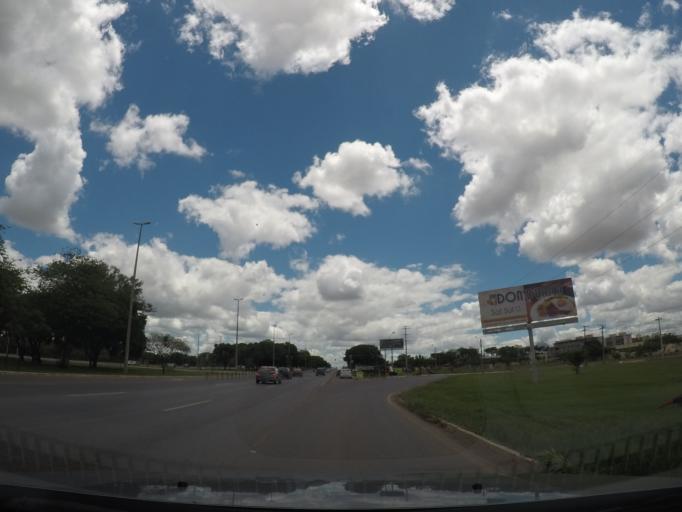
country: BR
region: Federal District
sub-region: Brasilia
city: Brasilia
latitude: -15.8192
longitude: -47.9502
